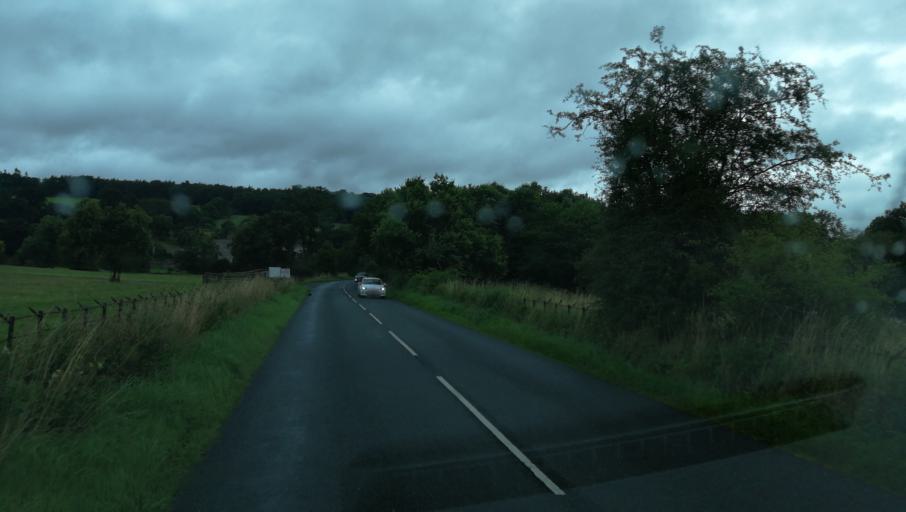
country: GB
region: England
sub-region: Cumbria
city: Penrith
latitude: 54.6313
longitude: -2.8110
